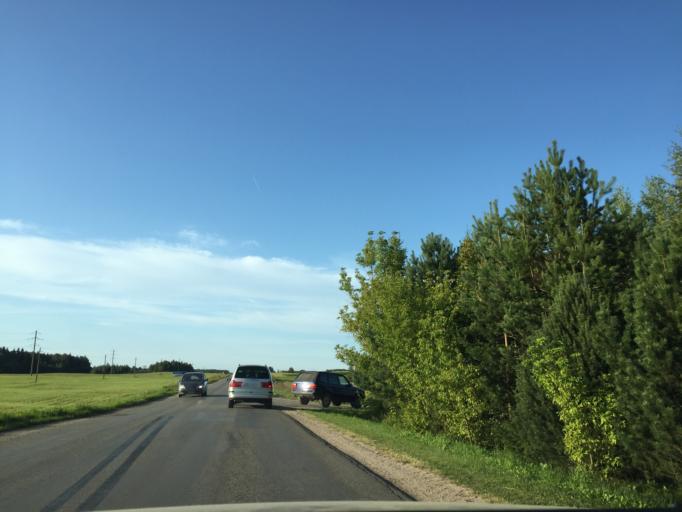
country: LT
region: Panevezys
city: Rokiskis
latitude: 55.9146
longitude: 25.6278
